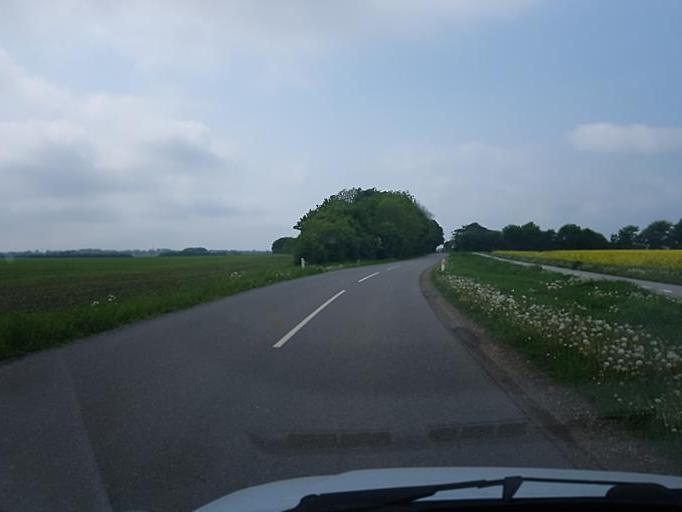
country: DK
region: South Denmark
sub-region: Varde Kommune
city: Varde
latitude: 55.5385
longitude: 8.5109
